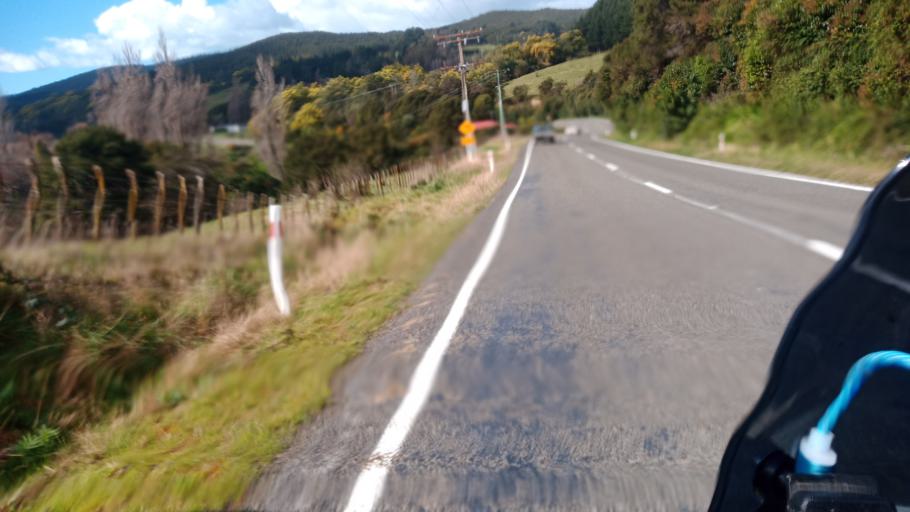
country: NZ
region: Gisborne
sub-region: Gisborne District
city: Gisborne
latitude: -37.9068
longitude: 178.2834
